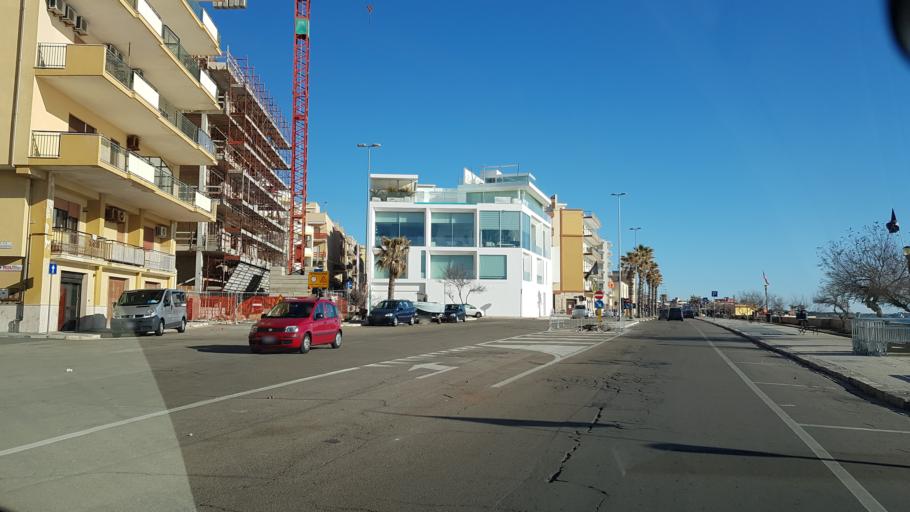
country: IT
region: Apulia
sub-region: Provincia di Lecce
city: Gallipoli
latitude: 40.0538
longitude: 17.9900
